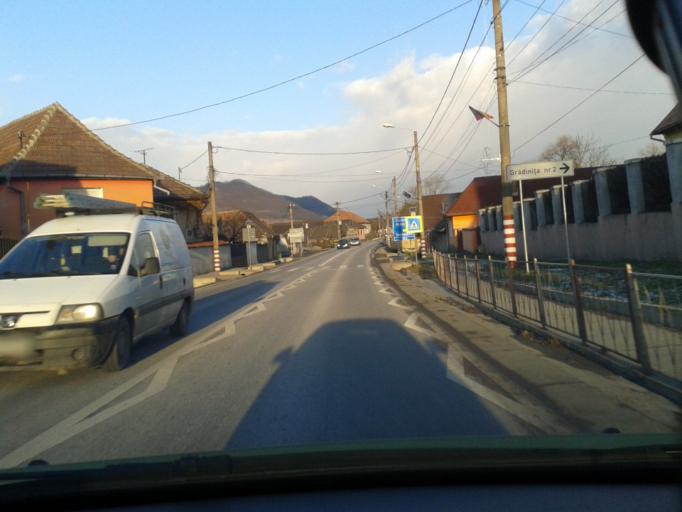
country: RO
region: Sibiu
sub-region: Comuna Copsa Mica
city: Copsa Mica
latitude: 46.1164
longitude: 24.2538
